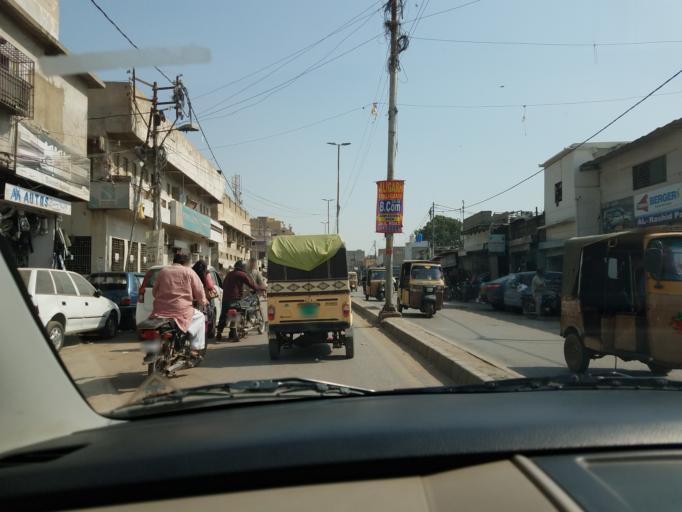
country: PK
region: Sindh
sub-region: Karachi District
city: Karachi
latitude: 24.8914
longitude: 67.0478
